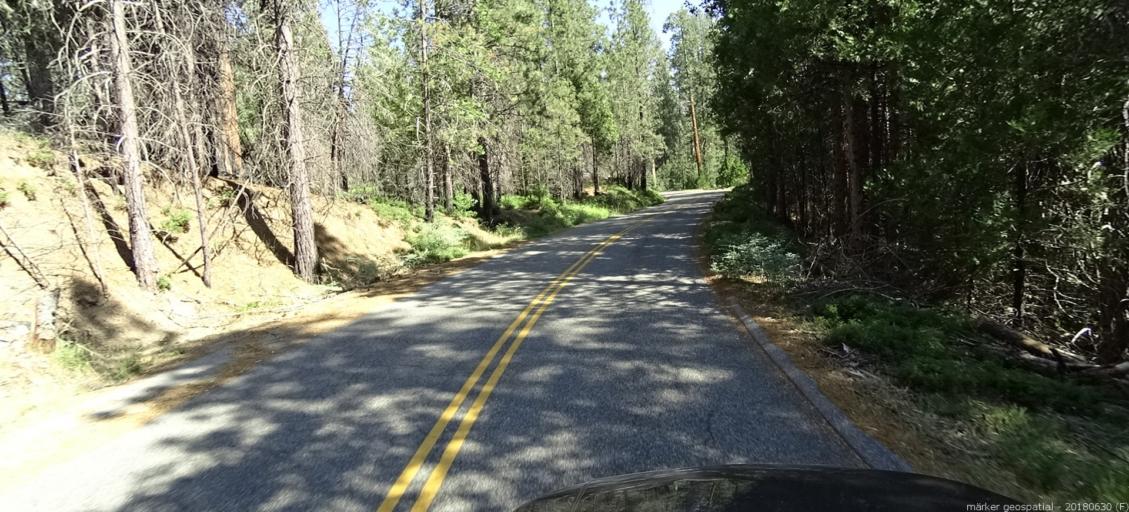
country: US
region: California
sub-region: Fresno County
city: Auberry
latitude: 37.2973
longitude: -119.3674
